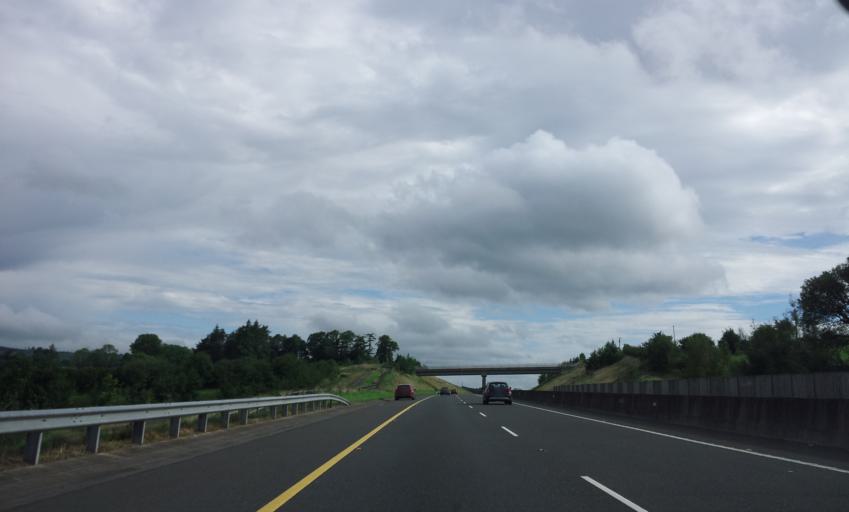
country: IE
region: Munster
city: Ballina
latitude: 52.7810
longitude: -8.3731
